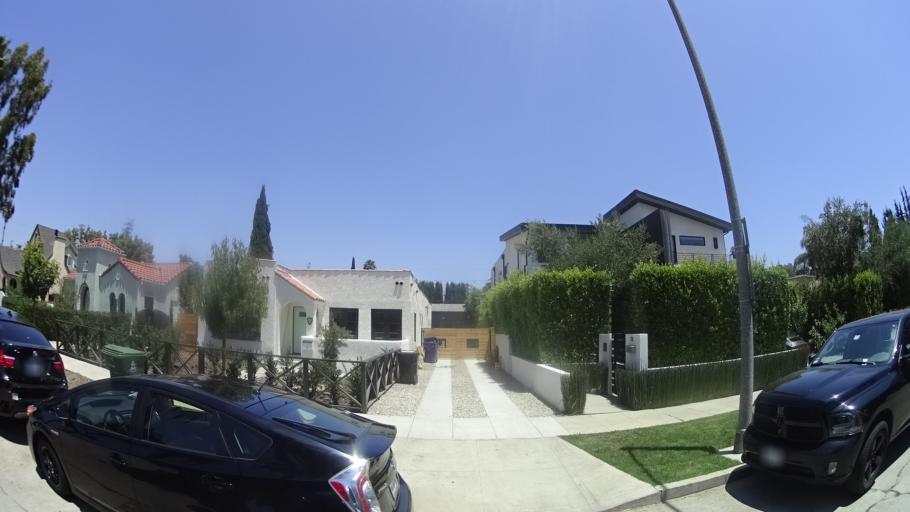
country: US
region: California
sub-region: Los Angeles County
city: Hollywood
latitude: 34.0844
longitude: -118.3375
